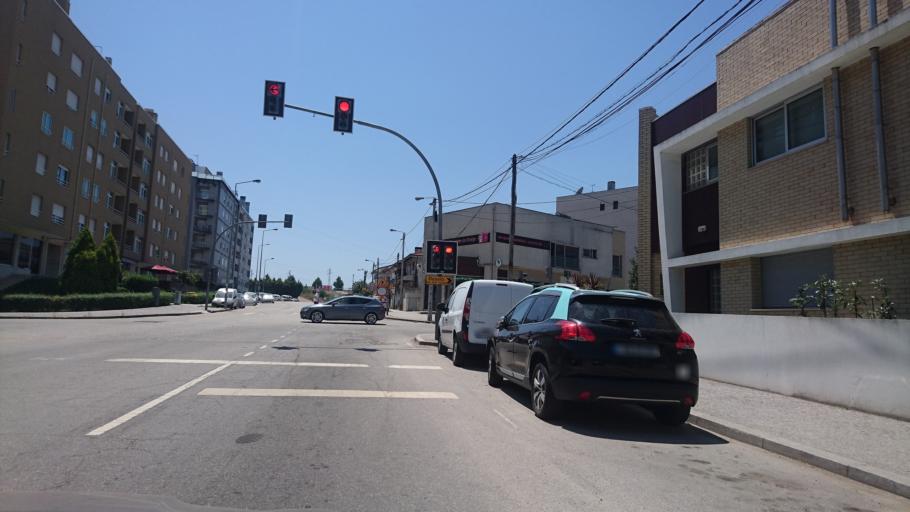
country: PT
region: Porto
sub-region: Valongo
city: Ermesinde
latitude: 41.2036
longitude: -8.5591
